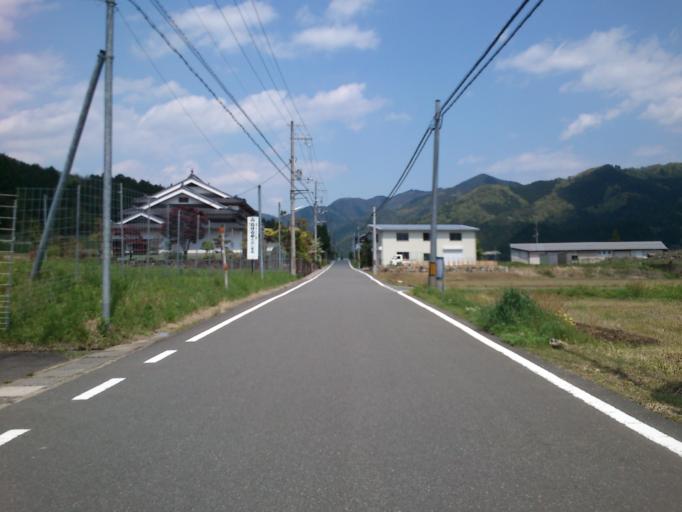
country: JP
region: Kyoto
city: Fukuchiyama
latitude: 35.3526
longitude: 134.9498
